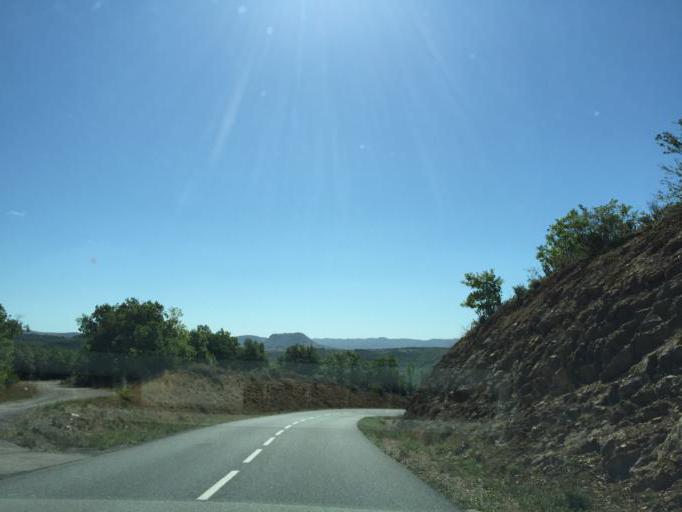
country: FR
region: Midi-Pyrenees
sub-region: Departement de l'Aveyron
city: Saint-Georges-de-Luzencon
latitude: 44.0711
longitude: 2.9044
